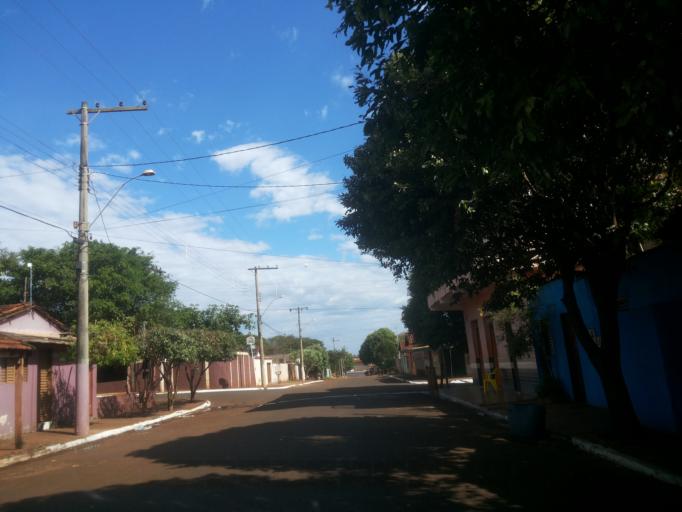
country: BR
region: Goias
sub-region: Itumbiara
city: Itumbiara
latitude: -18.4390
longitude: -49.1868
